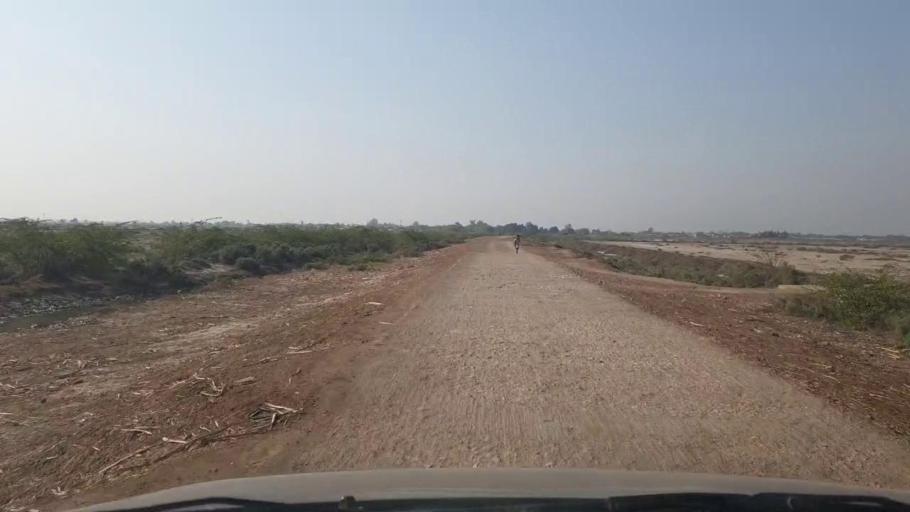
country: PK
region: Sindh
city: Mirwah Gorchani
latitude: 25.2862
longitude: 69.1411
